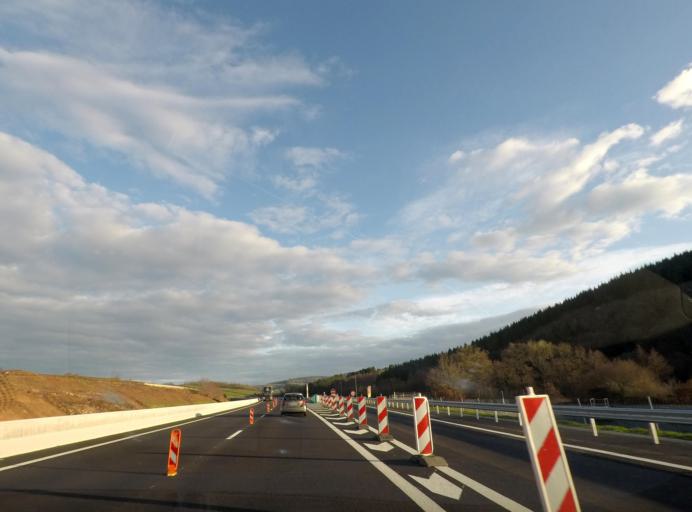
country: FR
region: Bourgogne
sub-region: Departement de Saone-et-Loire
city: Matour
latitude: 46.3732
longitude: 4.5397
